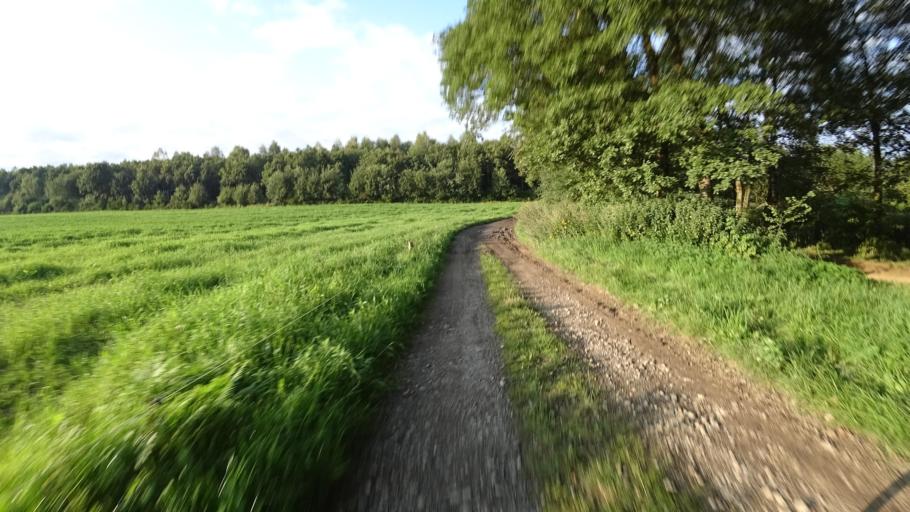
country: BE
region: Wallonia
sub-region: Province du Luxembourg
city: Neufchateau
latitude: 49.8702
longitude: 5.3750
